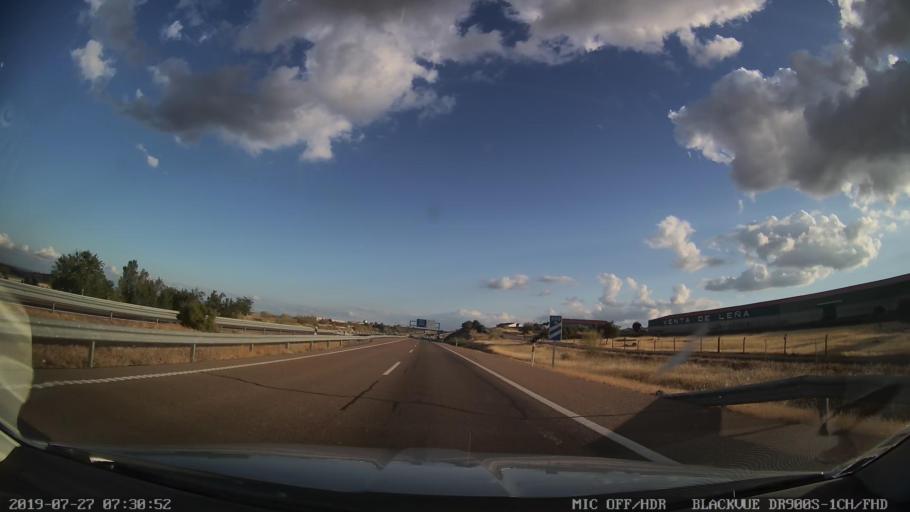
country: ES
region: Extremadura
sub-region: Provincia de Caceres
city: Escurial
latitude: 39.1815
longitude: -5.8969
